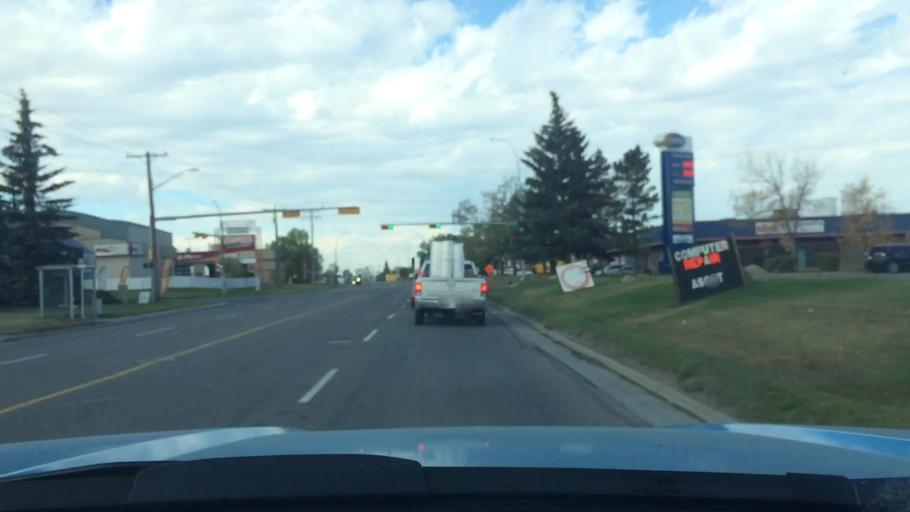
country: CA
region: Alberta
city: Calgary
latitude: 50.9991
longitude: -113.9798
